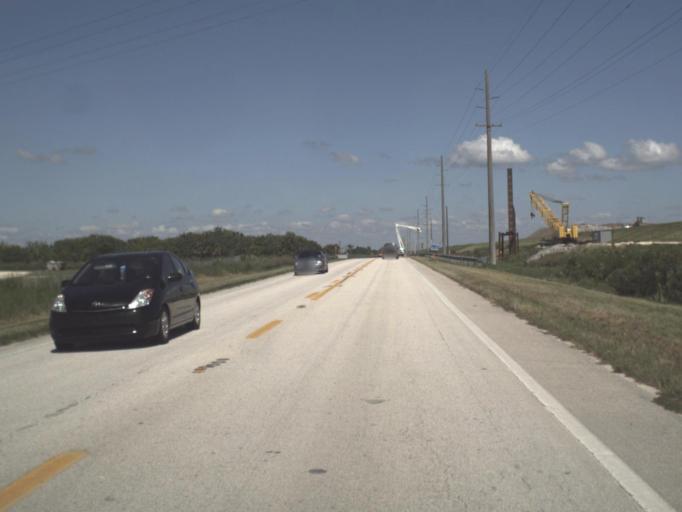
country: US
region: Florida
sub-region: Glades County
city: Moore Haven
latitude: 26.8837
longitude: -81.1225
